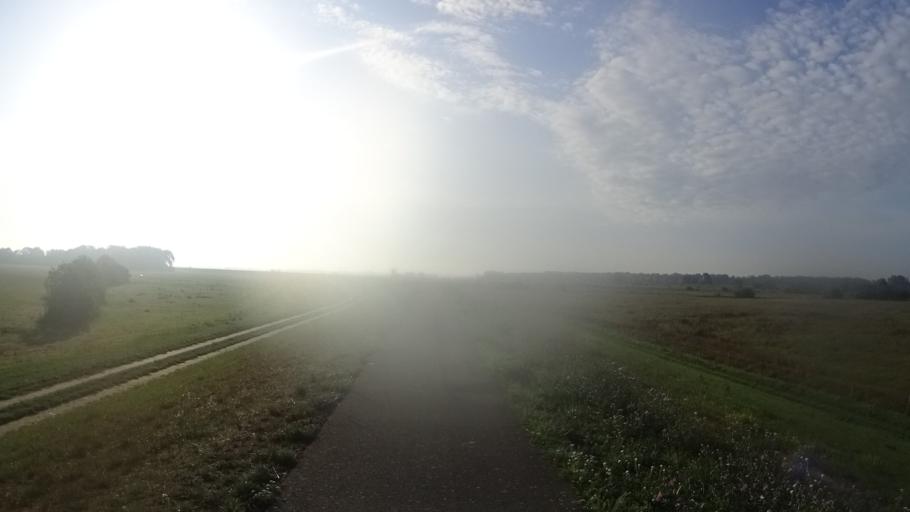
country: DE
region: Brandenburg
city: Lenzen
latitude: 53.0577
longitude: 11.5260
